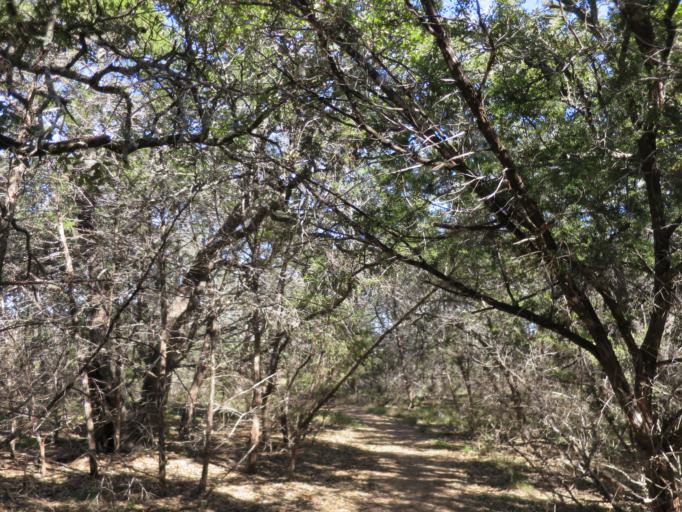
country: US
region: Texas
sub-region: Llano County
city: Kingsland
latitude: 30.6834
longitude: -98.3533
